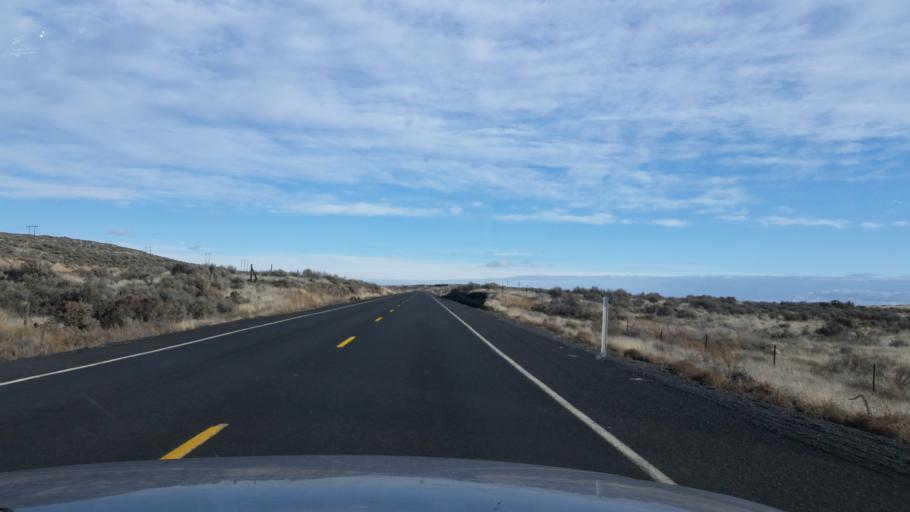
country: US
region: Washington
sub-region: Adams County
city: Ritzville
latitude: 47.3393
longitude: -118.6260
